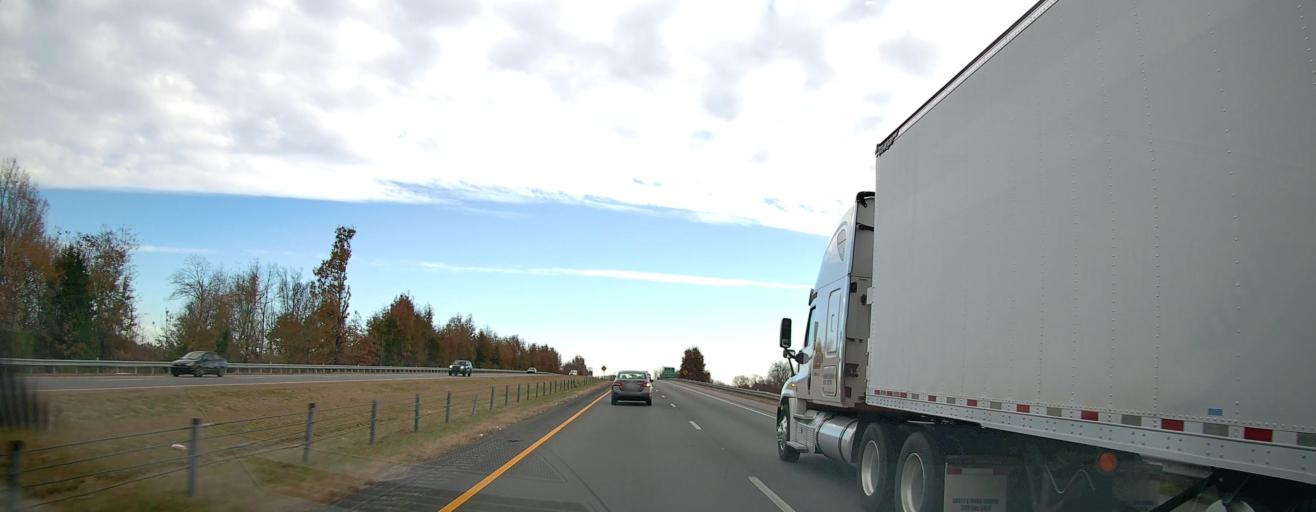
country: US
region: Alabama
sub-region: Morgan County
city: Decatur
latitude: 34.6492
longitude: -86.9091
